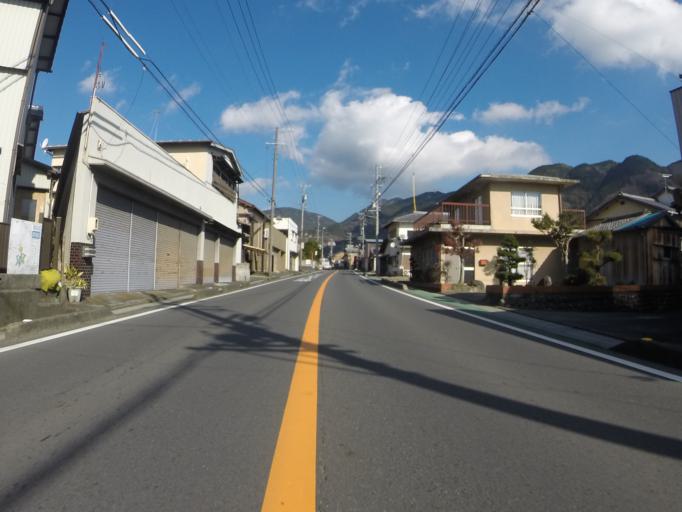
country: JP
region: Shizuoka
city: Fujinomiya
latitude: 35.0883
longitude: 138.5157
